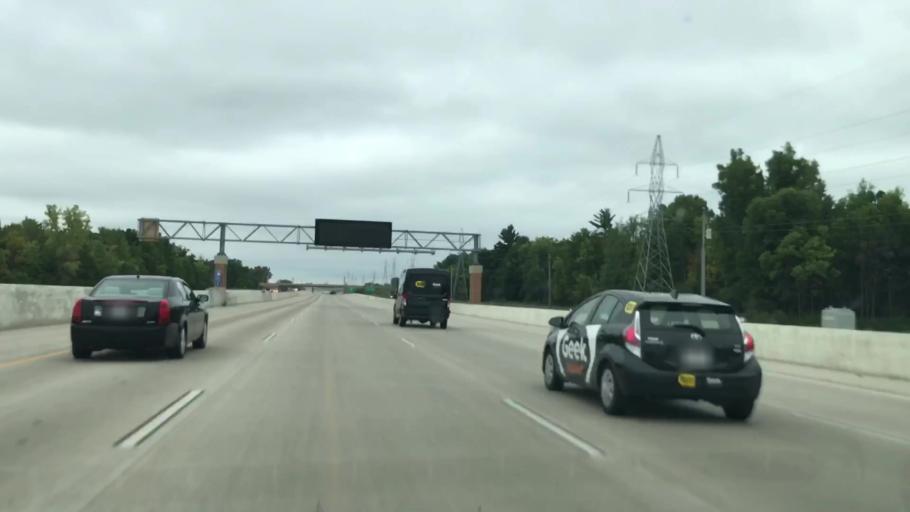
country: US
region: Wisconsin
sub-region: Brown County
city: Suamico
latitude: 44.5833
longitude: -88.0487
